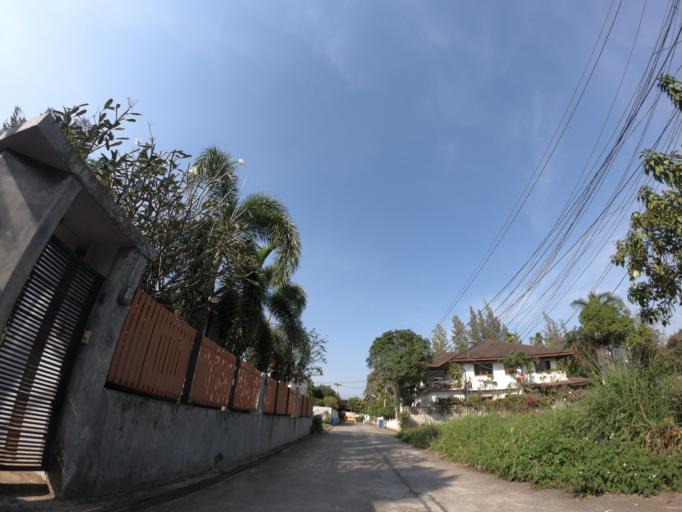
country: TH
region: Chiang Mai
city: Chiang Mai
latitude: 18.8193
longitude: 98.9881
